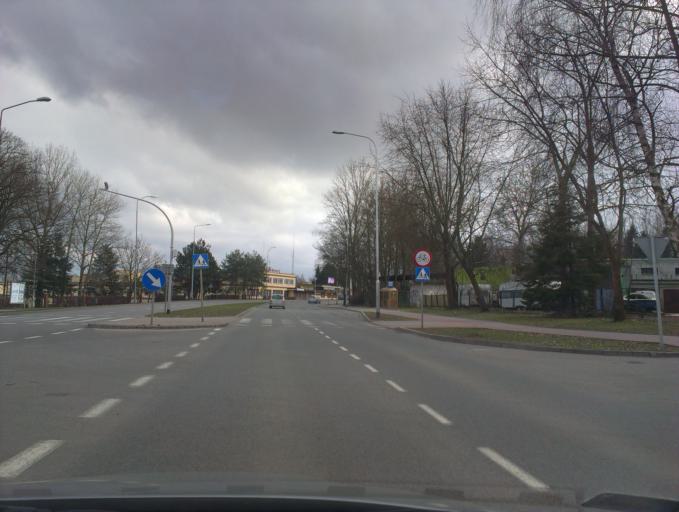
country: PL
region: West Pomeranian Voivodeship
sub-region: Koszalin
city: Koszalin
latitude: 54.1819
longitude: 16.1910
